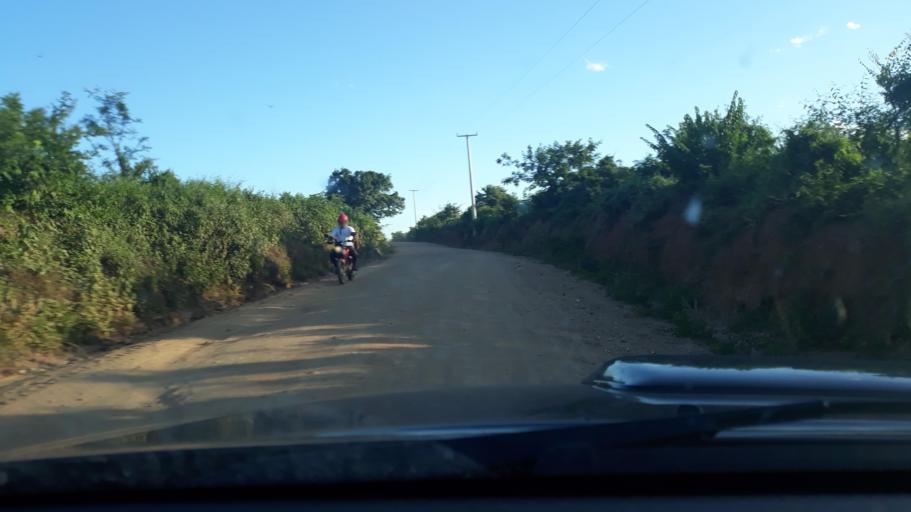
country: BR
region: Bahia
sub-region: Riacho De Santana
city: Riacho de Santana
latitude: -13.7912
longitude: -42.7122
